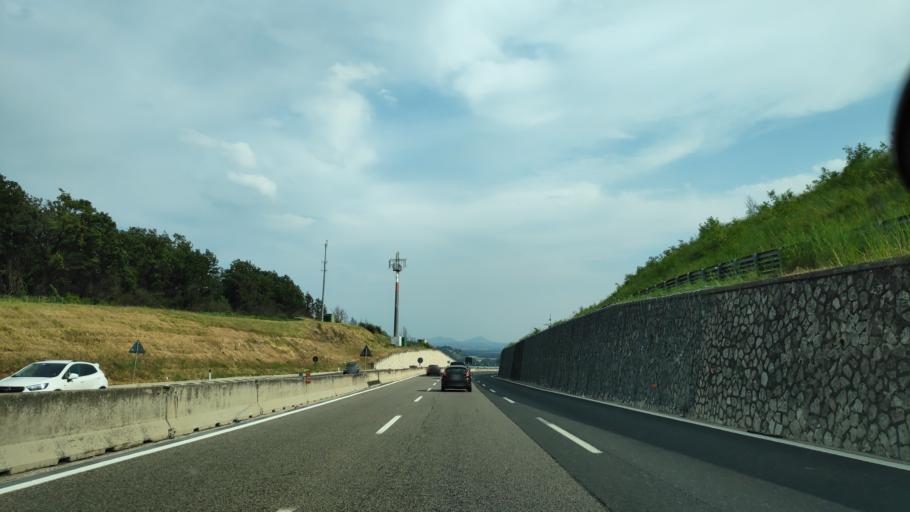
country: IT
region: Latium
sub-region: Citta metropolitana di Roma Capitale
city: Nazzano
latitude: 42.2090
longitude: 12.6022
